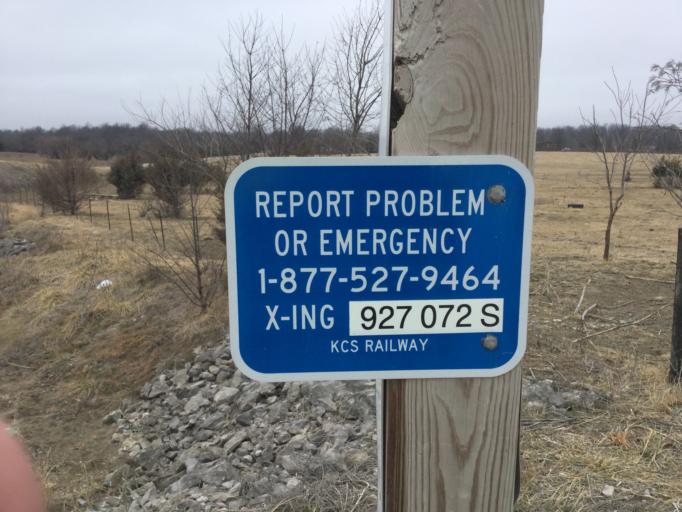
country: US
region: Kansas
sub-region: Crawford County
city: Pittsburg
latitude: 37.3604
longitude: -94.6500
